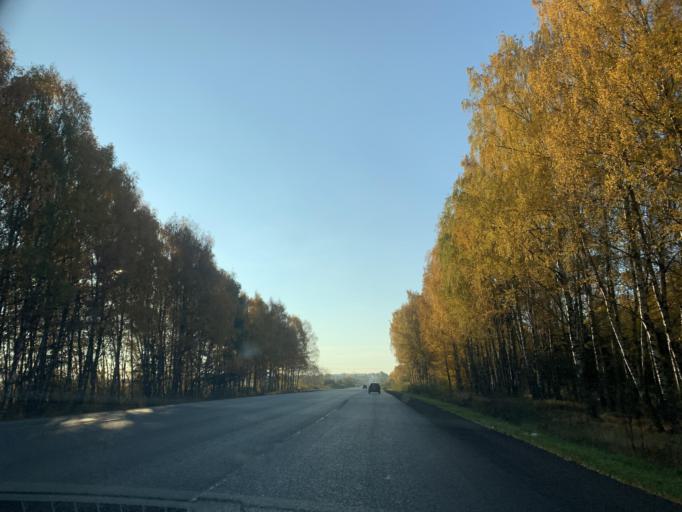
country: RU
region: Jaroslavl
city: Konstantinovskiy
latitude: 57.8020
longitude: 39.5931
